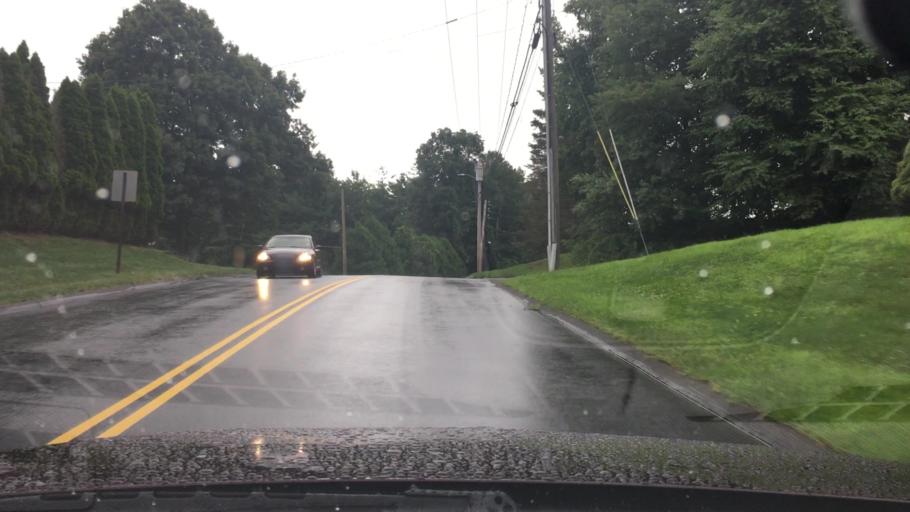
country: US
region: Connecticut
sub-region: New Haven County
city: Cheshire Village
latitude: 41.5294
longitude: -72.9169
